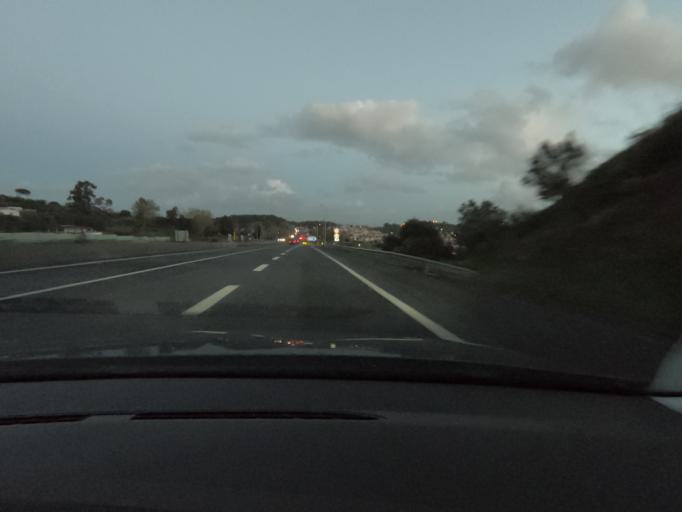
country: PT
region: Lisbon
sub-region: Oeiras
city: Quejas
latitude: 38.7191
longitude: -9.2711
